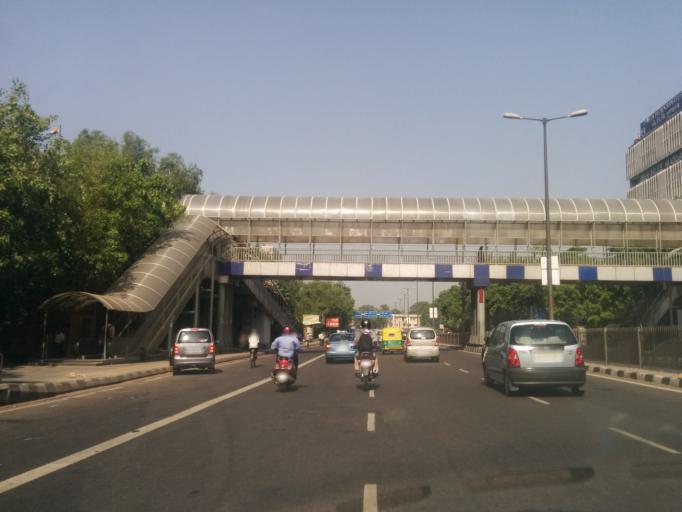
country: IN
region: NCT
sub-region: New Delhi
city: New Delhi
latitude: 28.6280
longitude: 77.2444
